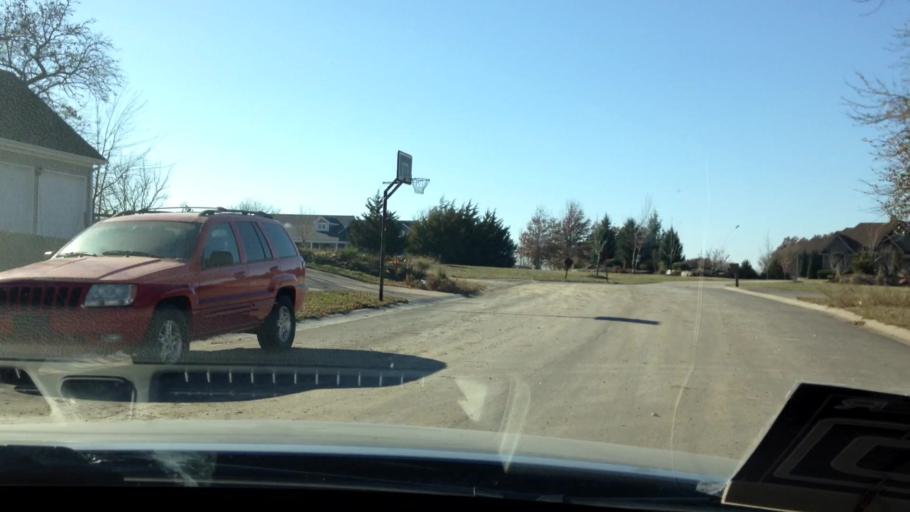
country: US
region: Kansas
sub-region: Johnson County
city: Olathe
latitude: 38.8914
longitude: -94.8665
